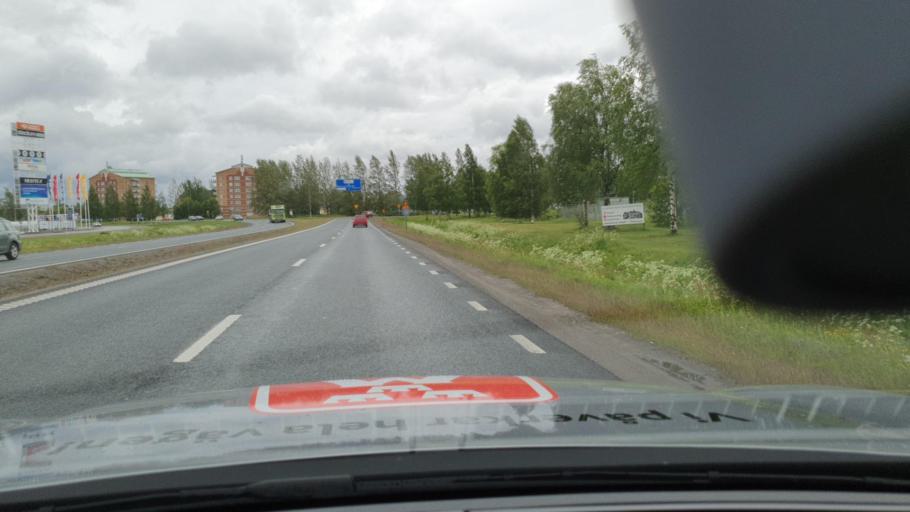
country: SE
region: Norrbotten
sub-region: Haparanda Kommun
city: Haparanda
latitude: 65.8438
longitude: 24.1254
